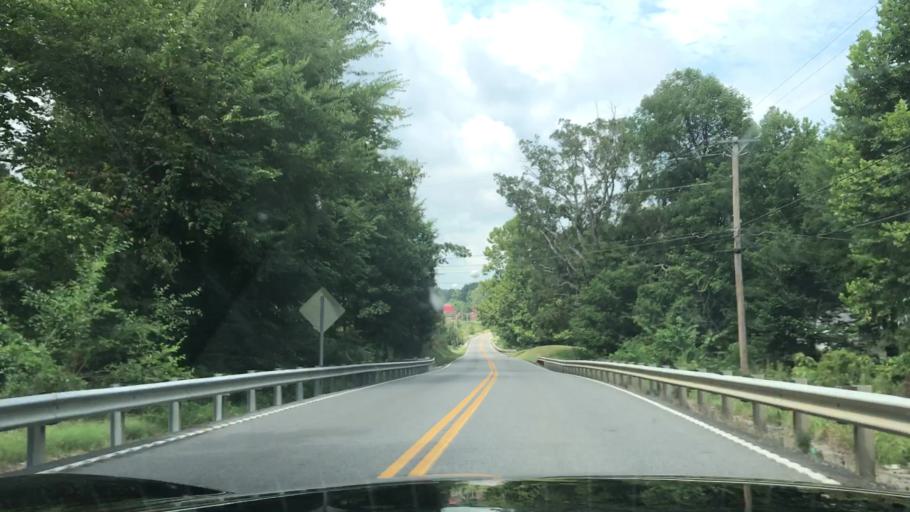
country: US
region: Kentucky
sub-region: Muhlenberg County
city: Greenville
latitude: 37.2056
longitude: -87.1591
